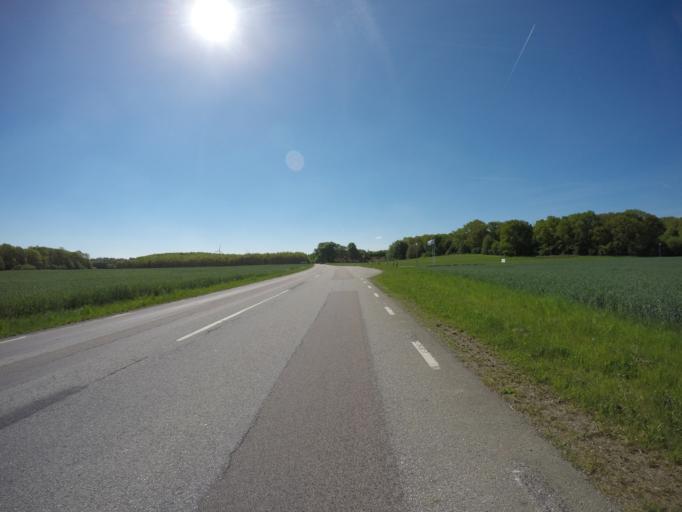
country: SE
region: Skane
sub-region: Malmo
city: Oxie
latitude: 55.5333
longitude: 13.1329
